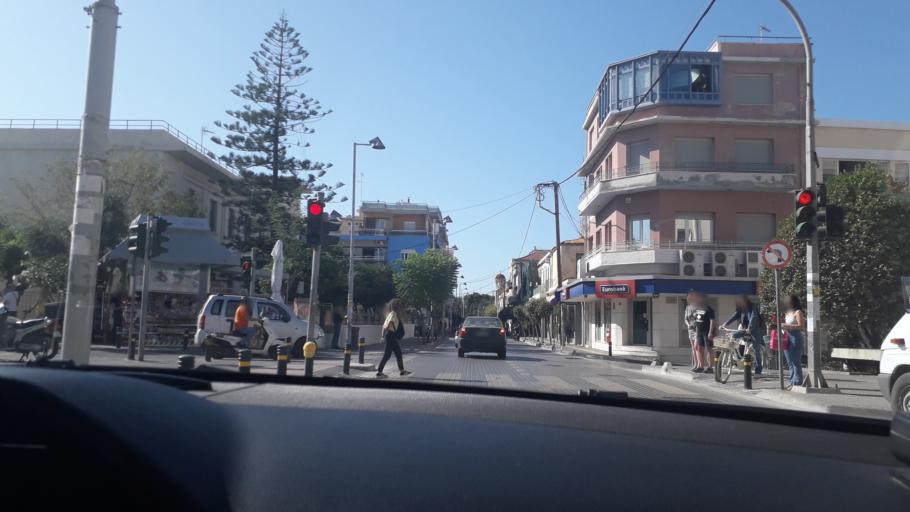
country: GR
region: Crete
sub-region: Nomos Rethymnis
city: Rethymno
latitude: 35.3661
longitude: 24.4776
